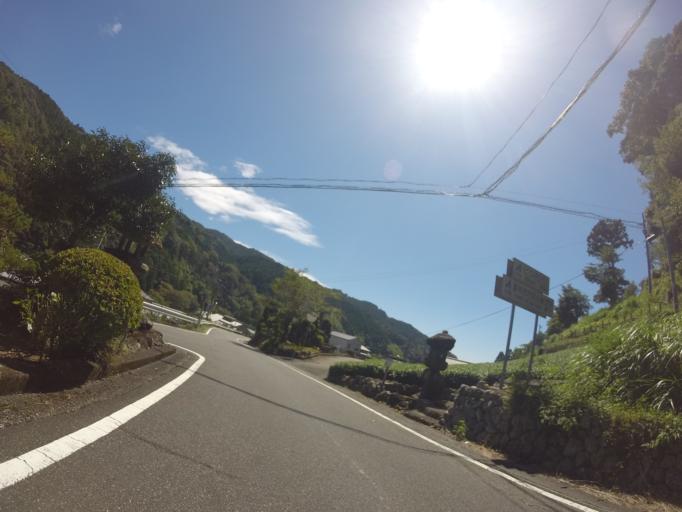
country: JP
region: Shizuoka
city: Fujieda
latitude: 34.9696
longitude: 138.2118
